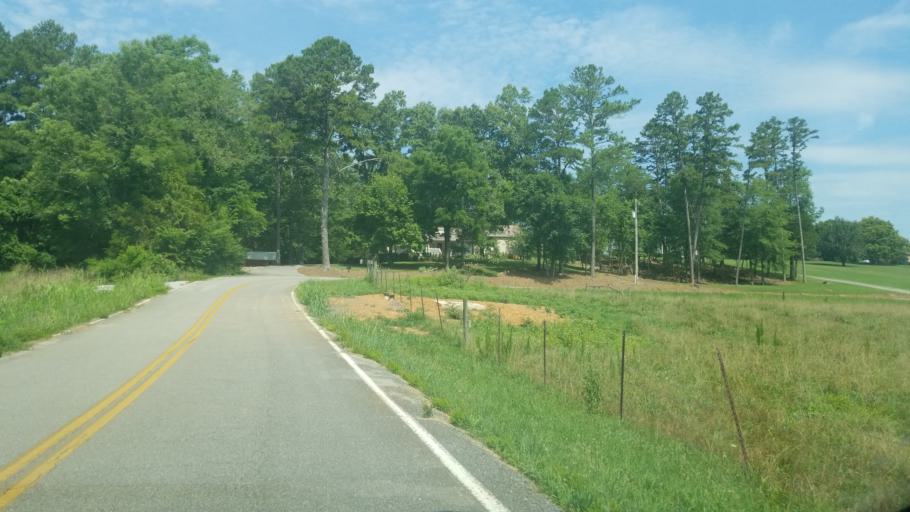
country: US
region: Tennessee
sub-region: Hamilton County
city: Lakesite
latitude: 35.2188
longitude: -85.0173
